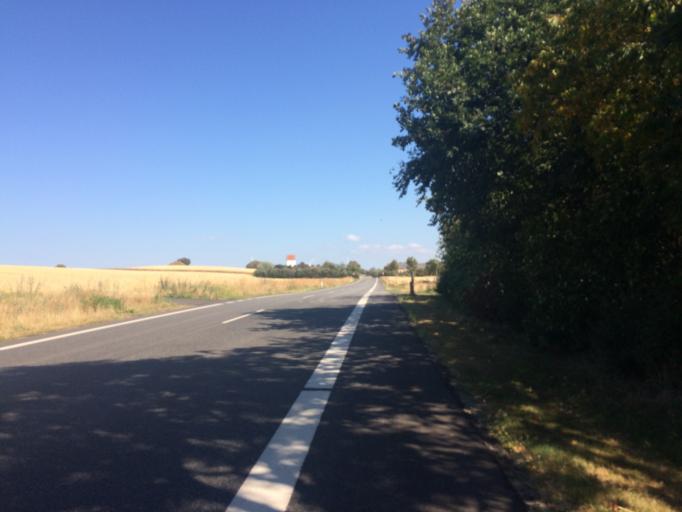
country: DK
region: Central Jutland
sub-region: Holstebro Kommune
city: Vinderup
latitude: 56.5804
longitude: 8.8383
